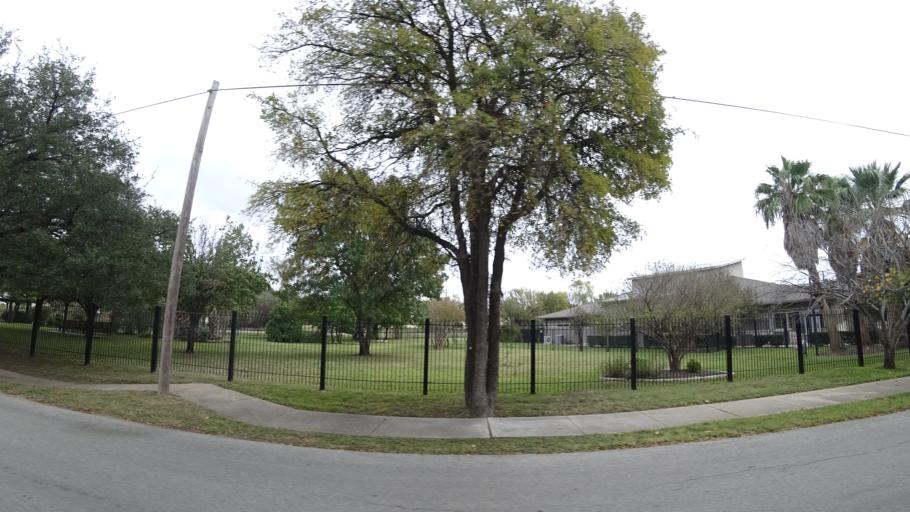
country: US
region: Texas
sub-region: Williamson County
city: Round Rock
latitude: 30.5095
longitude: -97.6896
